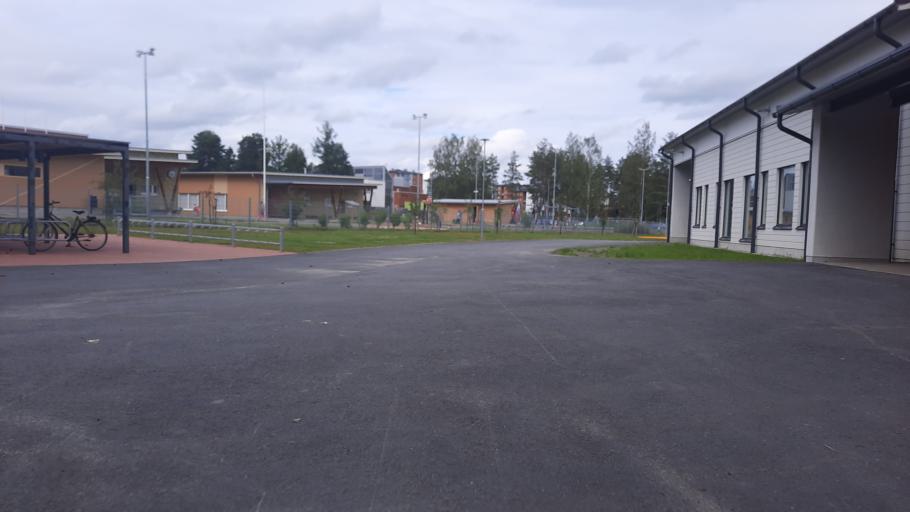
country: FI
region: North Karelia
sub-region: Joensuu
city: Joensuu
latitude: 62.6130
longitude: 29.8193
